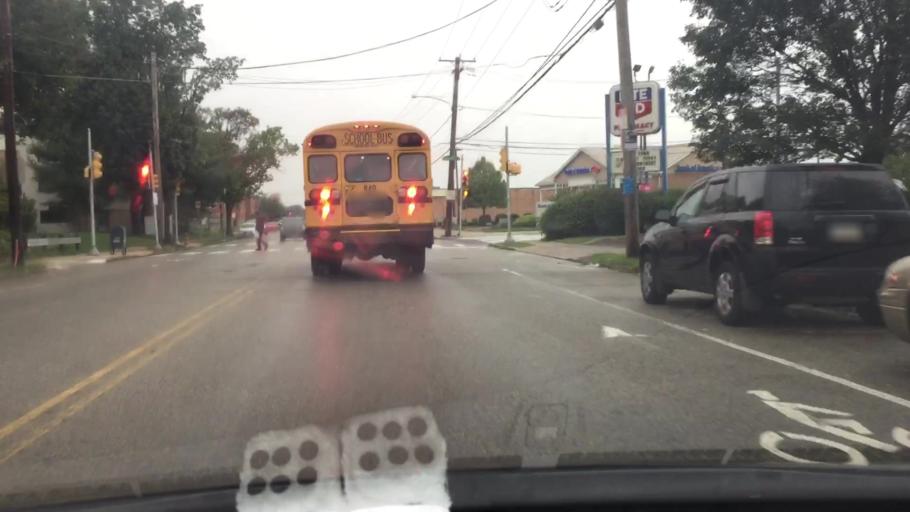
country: US
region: Pennsylvania
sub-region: Montgomery County
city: Rockledge
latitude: 40.0699
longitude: -75.0310
